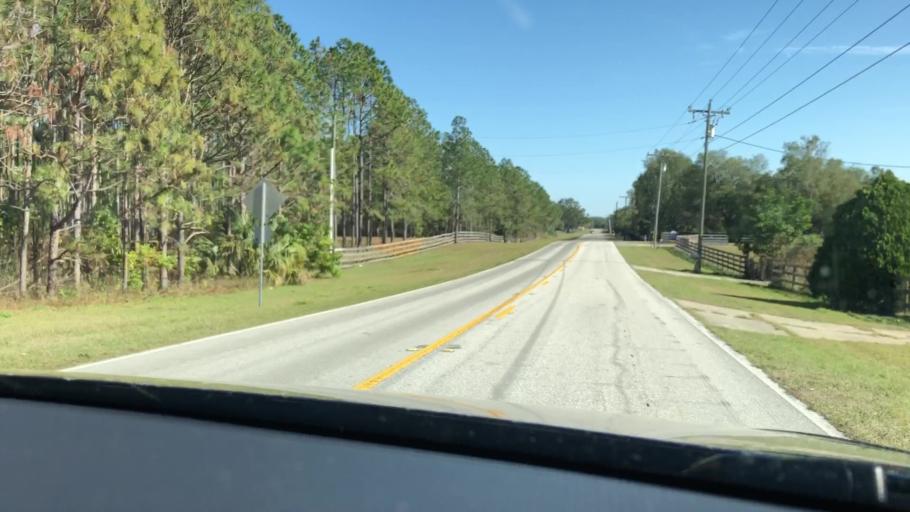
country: US
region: Florida
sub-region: Lake County
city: Eustis
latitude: 28.8732
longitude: -81.6144
